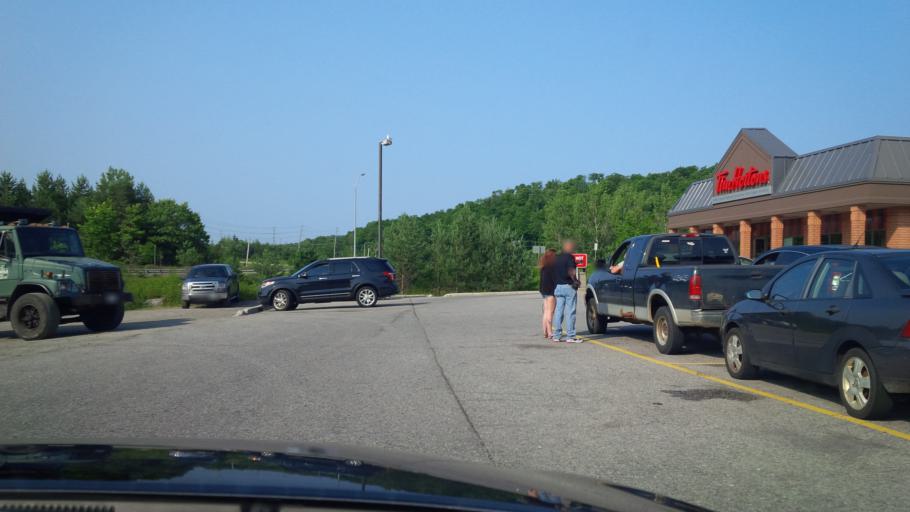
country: CA
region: Ontario
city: Huntsville
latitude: 45.3321
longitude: -79.2341
